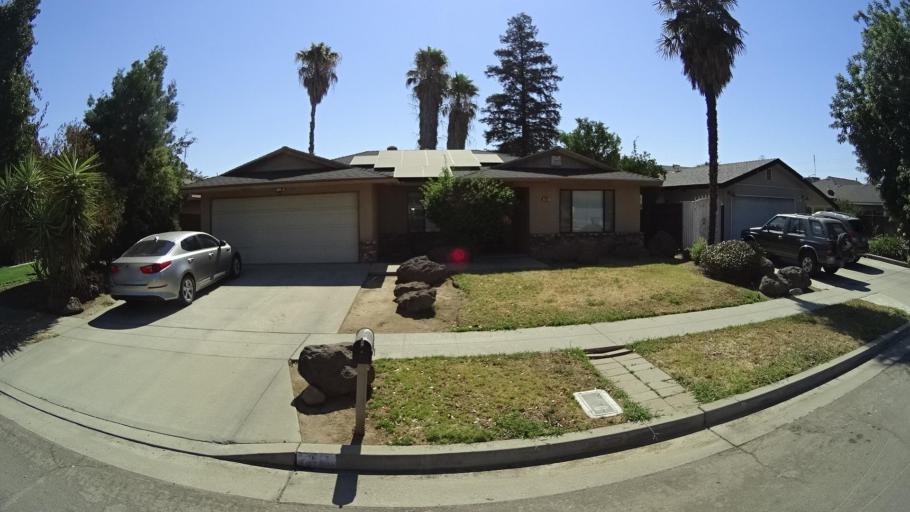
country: US
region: California
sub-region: Fresno County
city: Sunnyside
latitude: 36.7468
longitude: -119.6884
